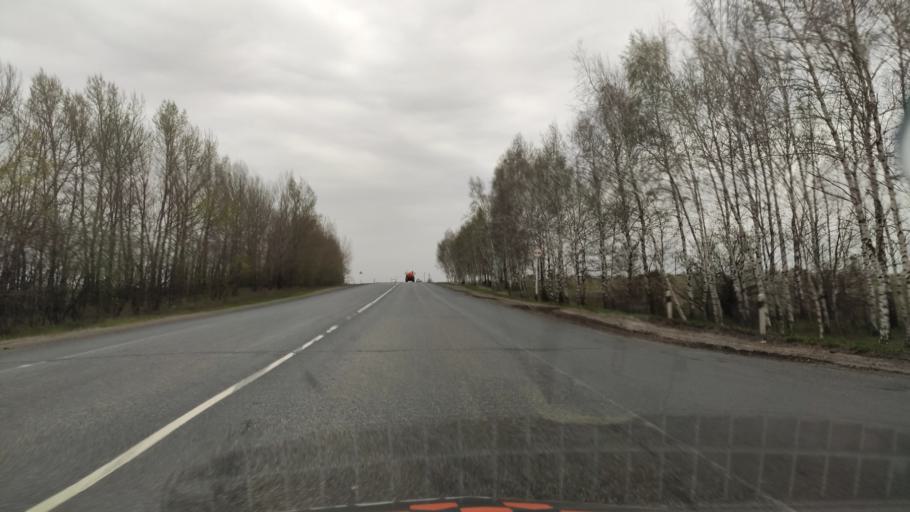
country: RU
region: Kursk
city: Gorshechnoye
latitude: 51.4835
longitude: 37.9621
